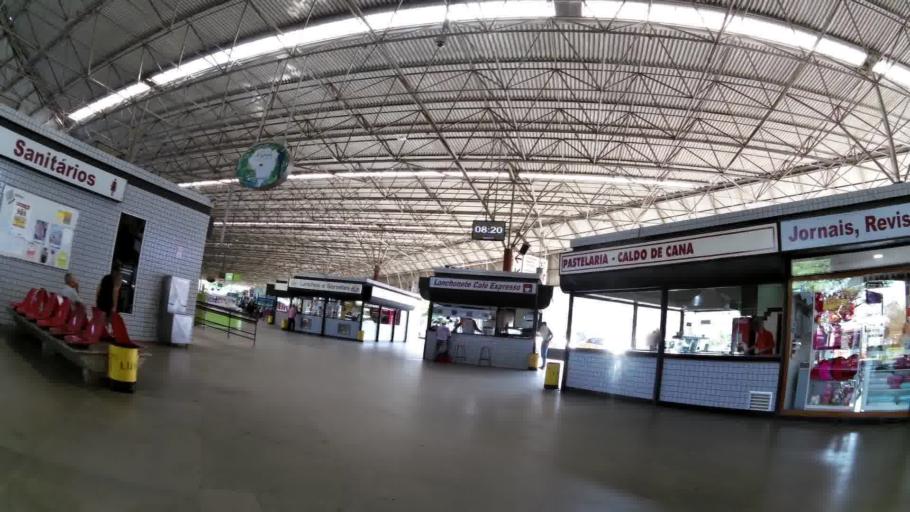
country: BR
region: Espirito Santo
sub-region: Vitoria
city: Vitoria
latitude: -20.3223
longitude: -40.3516
